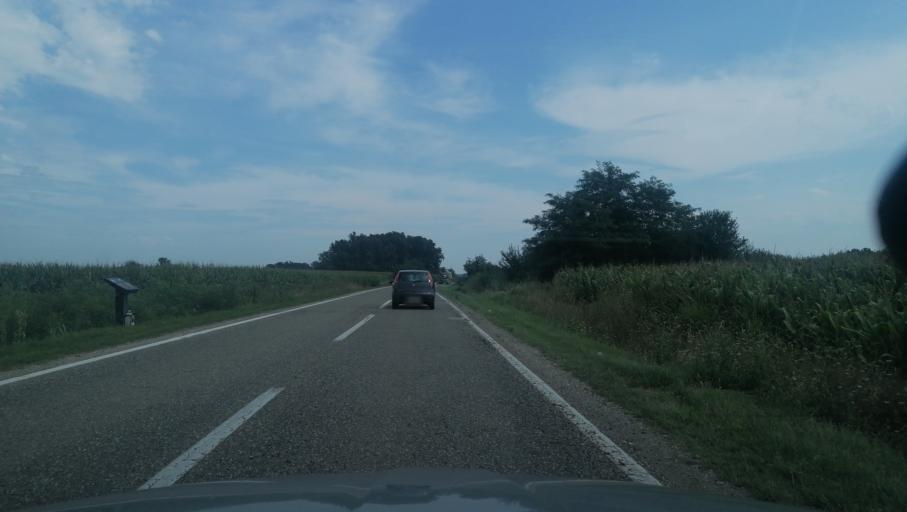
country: HR
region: Vukovarsko-Srijemska
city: Soljani
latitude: 44.8321
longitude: 18.9959
